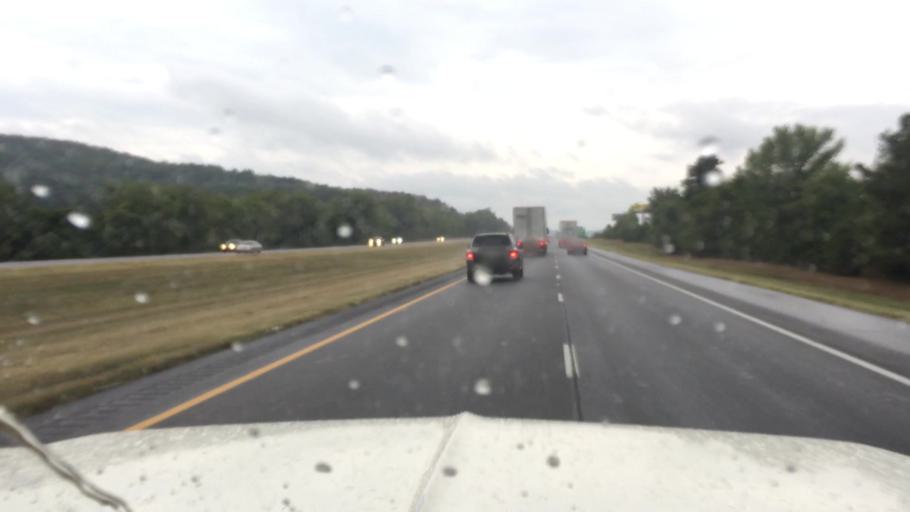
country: US
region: Alabama
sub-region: Morgan County
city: Falkville
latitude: 34.3922
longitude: -86.8958
